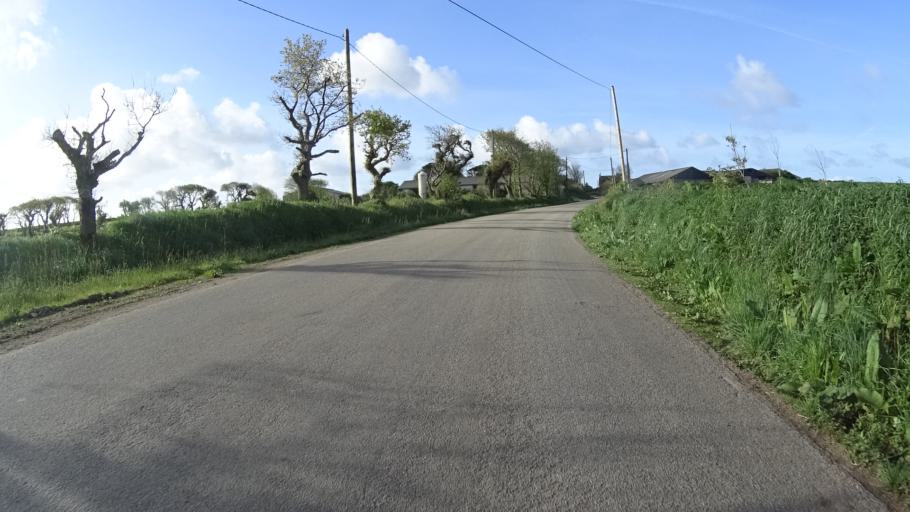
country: FR
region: Brittany
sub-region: Departement du Finistere
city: Plouzane
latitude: 48.3983
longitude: -4.6648
